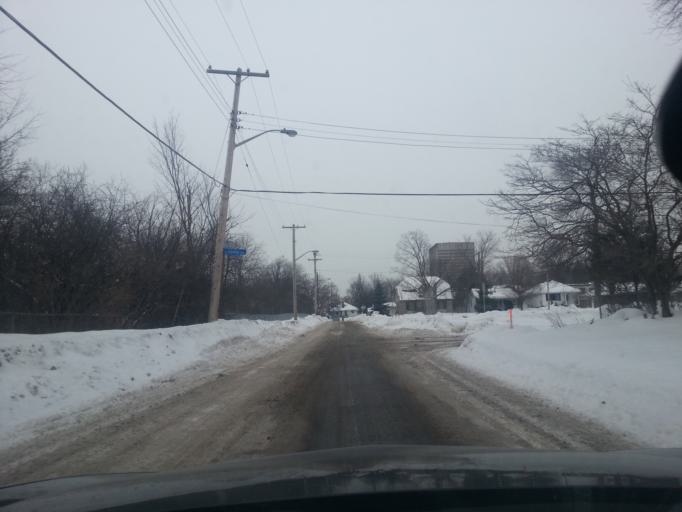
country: CA
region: Ontario
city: Ottawa
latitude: 45.4053
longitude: -75.7466
